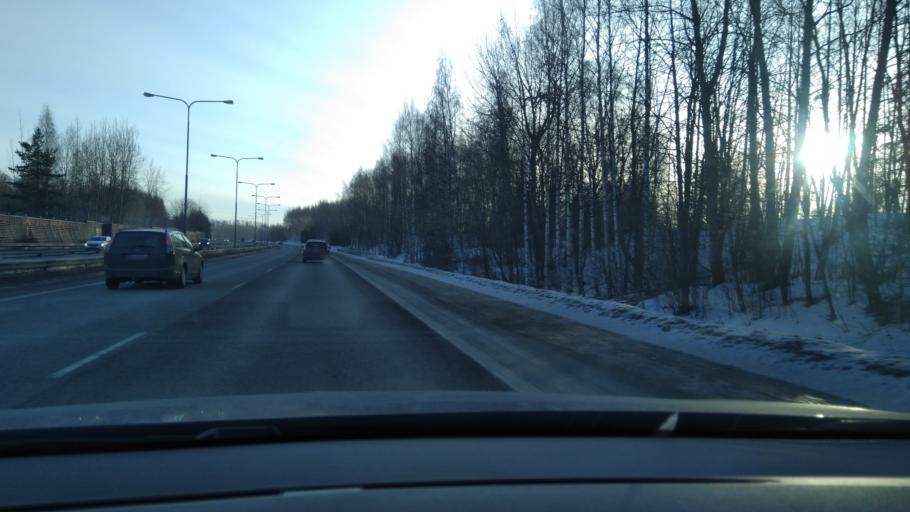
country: FI
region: Pirkanmaa
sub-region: Tampere
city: Pirkkala
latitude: 61.5004
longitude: 23.6710
